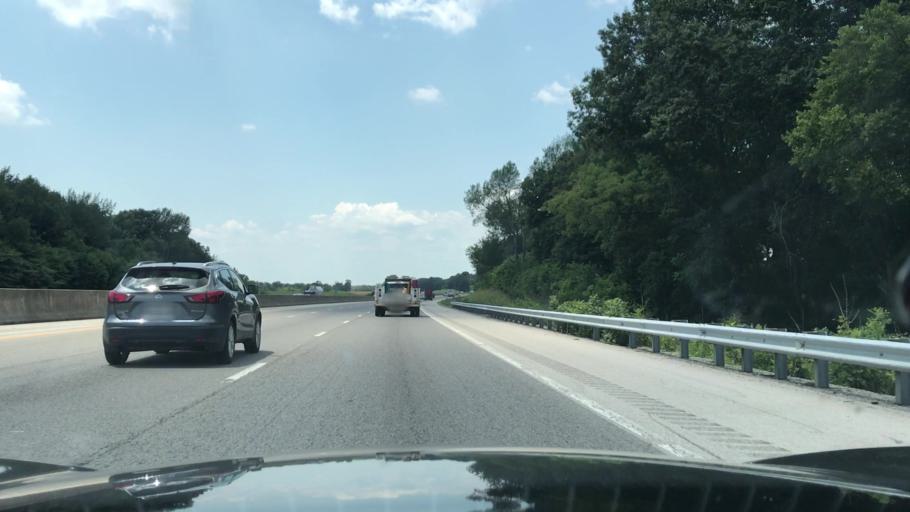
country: US
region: Kentucky
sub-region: Edmonson County
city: Brownsville
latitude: 37.0423
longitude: -86.1778
